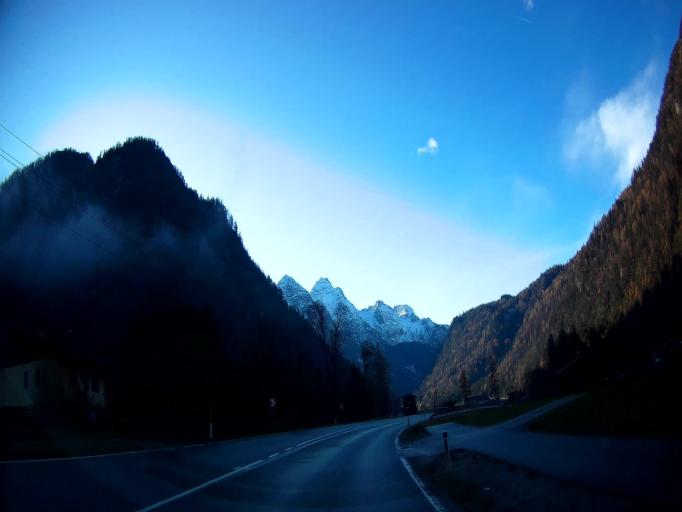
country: AT
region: Salzburg
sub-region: Politischer Bezirk Zell am See
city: Sankt Martin bei Lofer
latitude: 47.5533
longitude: 12.7265
